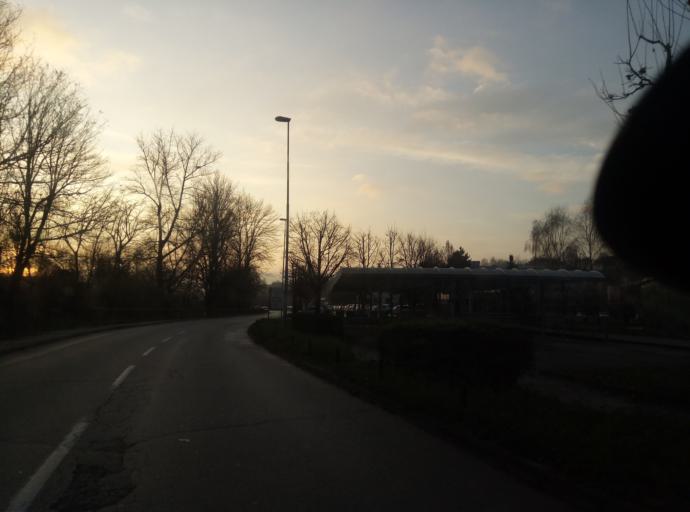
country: SI
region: Kranj
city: Kranj
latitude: 46.2377
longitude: 14.3515
